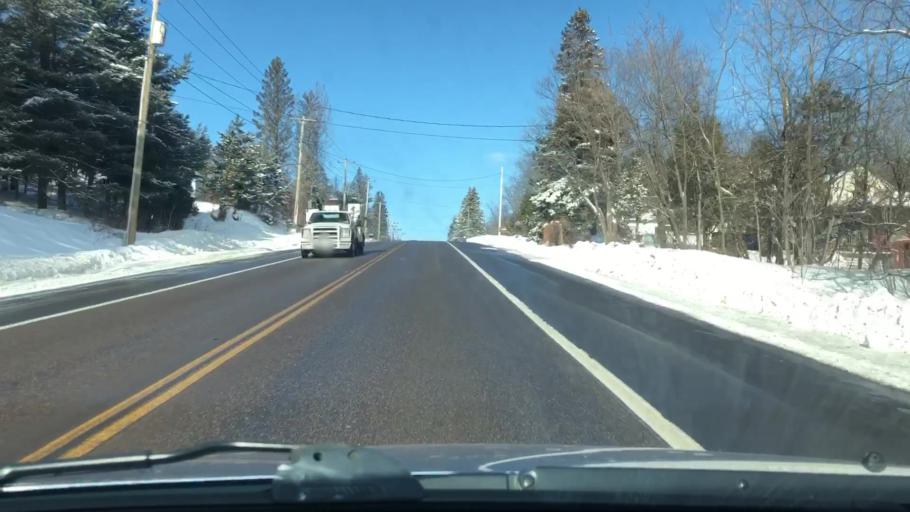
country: US
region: Minnesota
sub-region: Saint Louis County
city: Duluth
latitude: 46.8117
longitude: -92.1322
